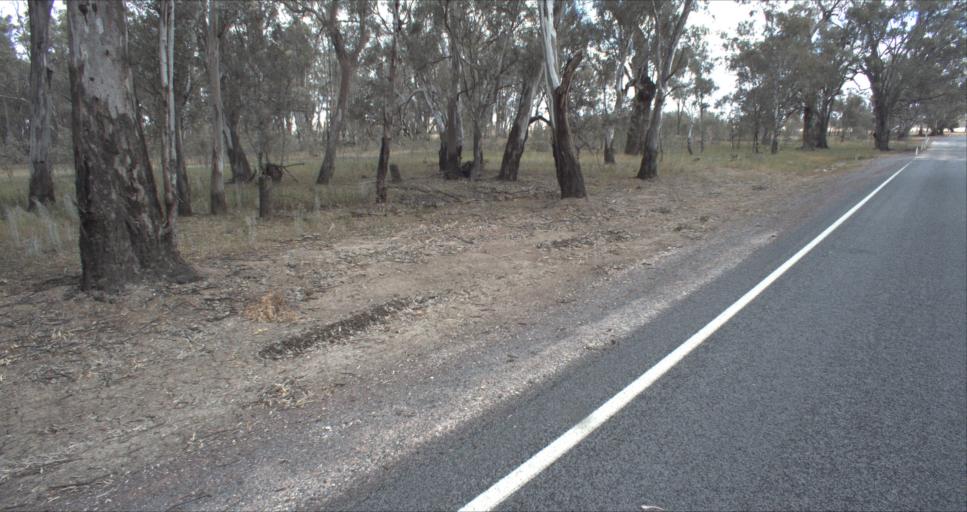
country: AU
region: New South Wales
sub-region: Leeton
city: Leeton
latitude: -34.6419
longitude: 146.3582
